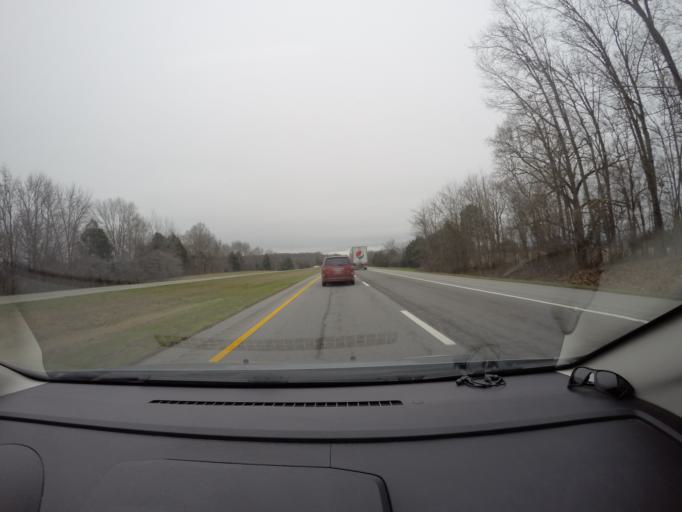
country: US
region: Tennessee
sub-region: Franklin County
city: Sewanee
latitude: 35.3473
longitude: -85.9459
